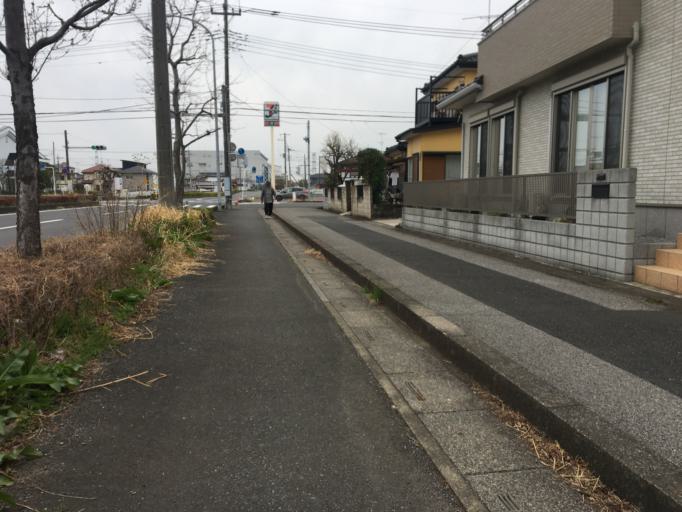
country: JP
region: Saitama
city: Kisai
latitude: 36.0996
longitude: 139.5818
